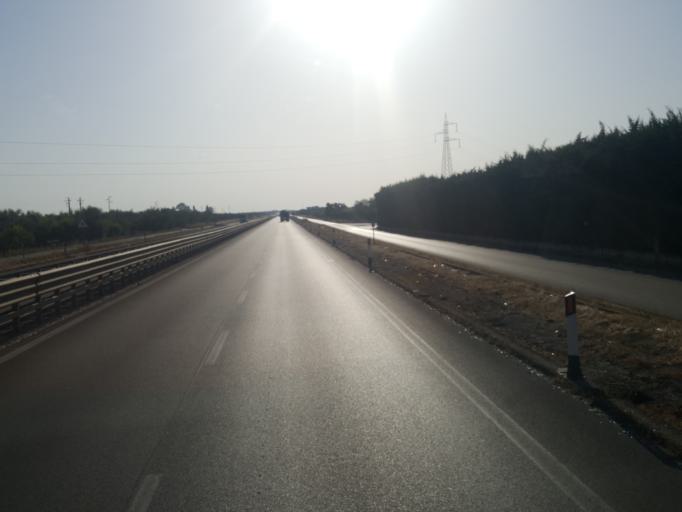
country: IT
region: Apulia
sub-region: Provincia di Barletta - Andria - Trani
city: San Ferdinando di Puglia
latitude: 41.3136
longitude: 16.1066
